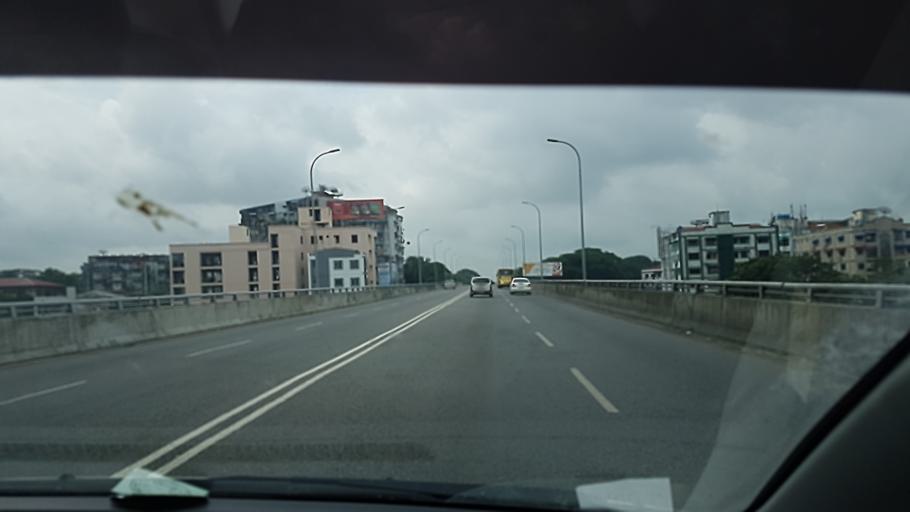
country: MM
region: Yangon
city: Yangon
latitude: 16.8038
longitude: 96.1373
